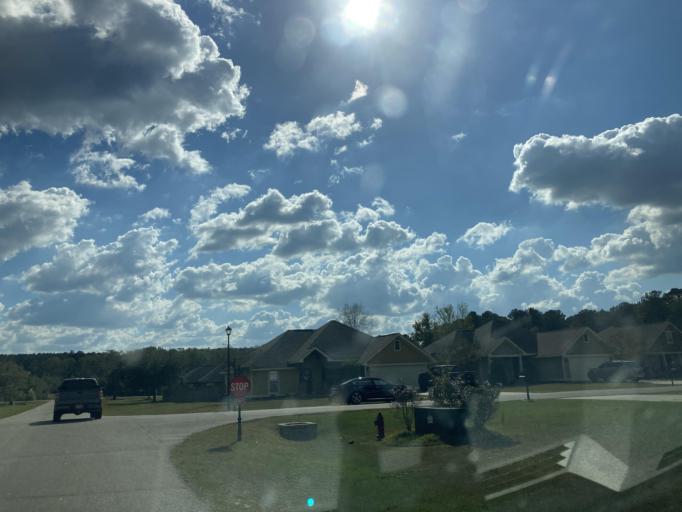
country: US
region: Mississippi
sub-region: Lamar County
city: Sumrall
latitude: 31.4273
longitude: -89.5337
